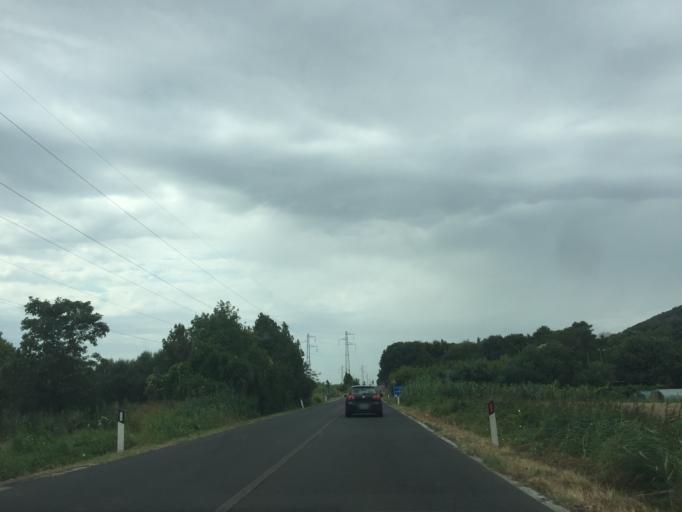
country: IT
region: Tuscany
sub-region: Province of Pisa
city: Gabella
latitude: 43.7308
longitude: 10.4821
